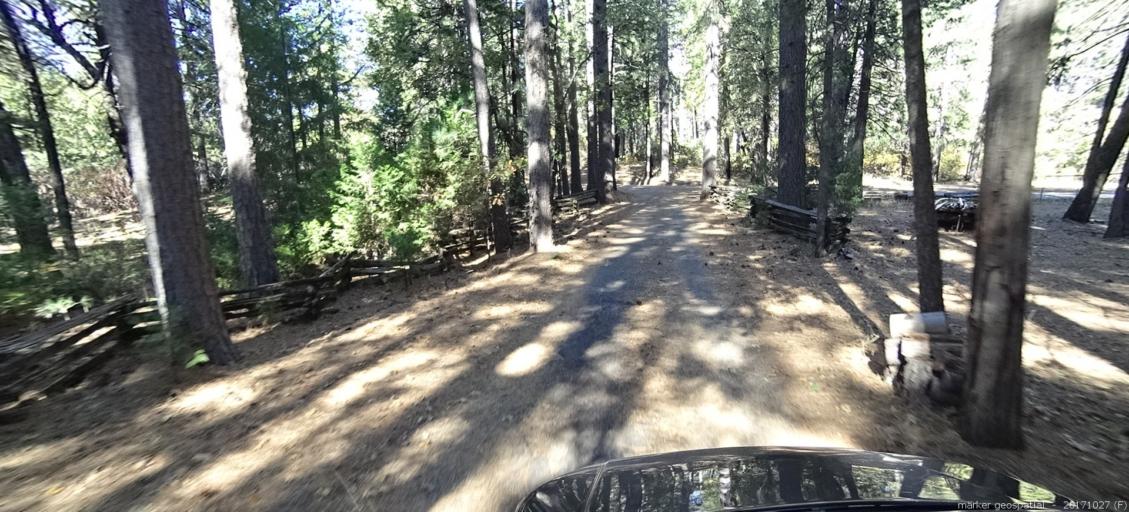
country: US
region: California
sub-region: Shasta County
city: Burney
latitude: 40.8042
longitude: -121.8978
